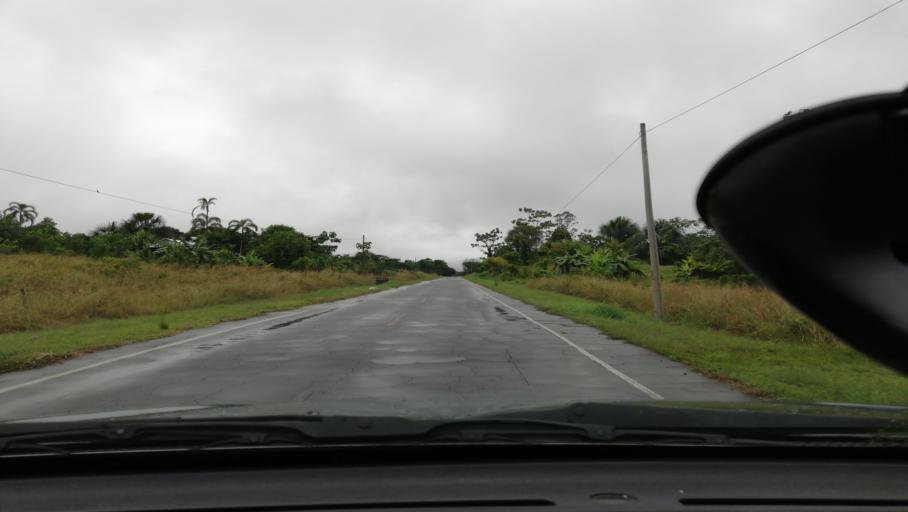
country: PE
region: Loreto
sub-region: Provincia de Loreto
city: Nauta
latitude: -4.2573
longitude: -73.5013
